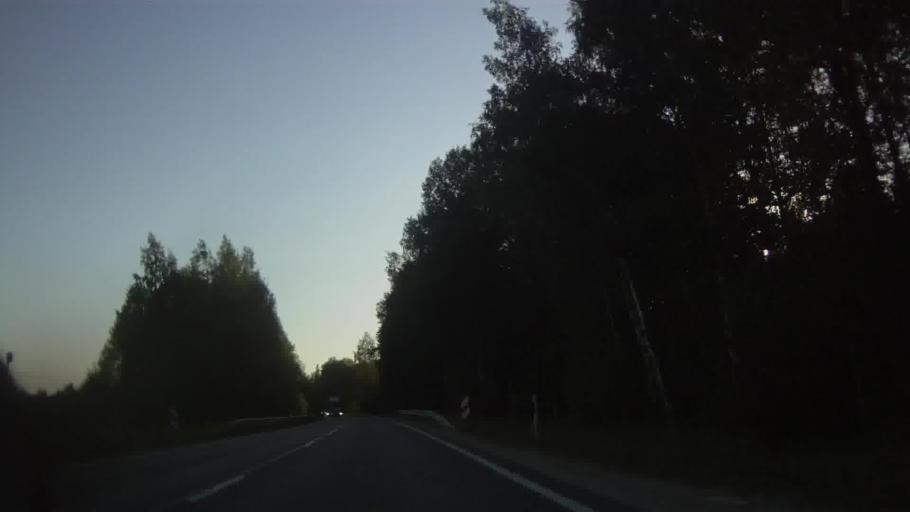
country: LV
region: Livani
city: Livani
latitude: 56.5288
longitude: 26.2079
